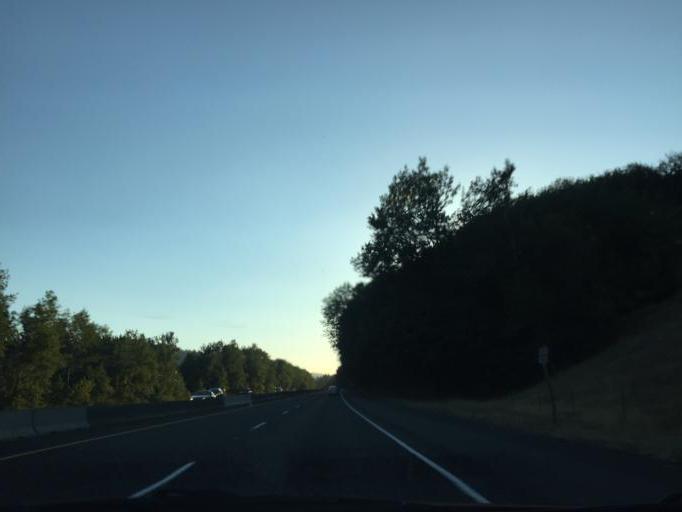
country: US
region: Washington
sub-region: Clark County
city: Washougal
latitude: 45.5486
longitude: -122.2041
